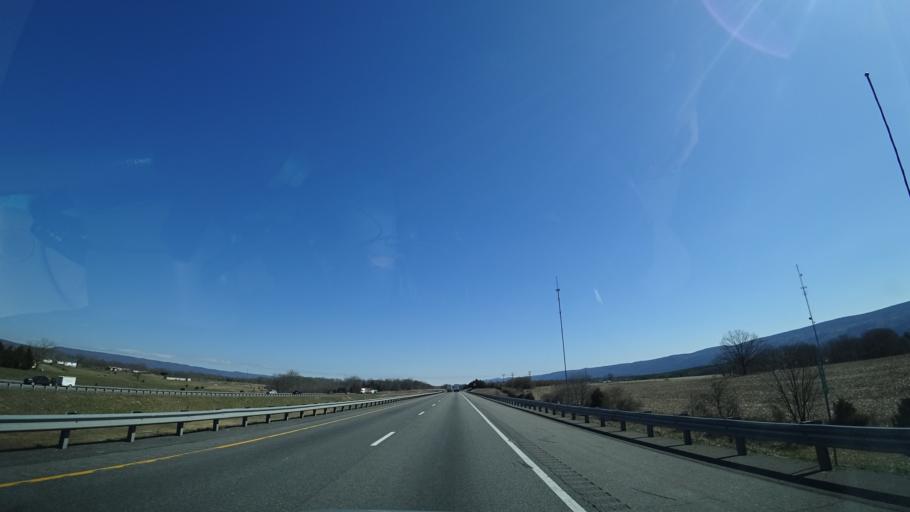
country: US
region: Virginia
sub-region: Shenandoah County
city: Edinburg
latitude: 38.8406
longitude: -78.5601
